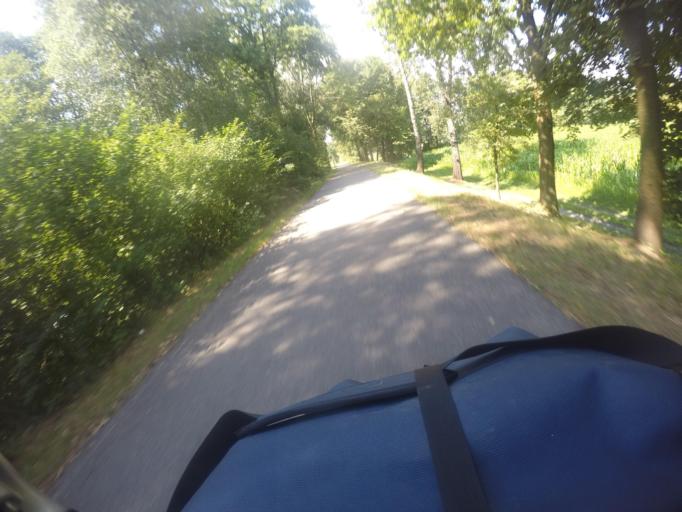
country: CH
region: Saint Gallen
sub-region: Wahlkreis Rheintal
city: Diepoldsau
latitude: 47.3904
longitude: 9.6760
